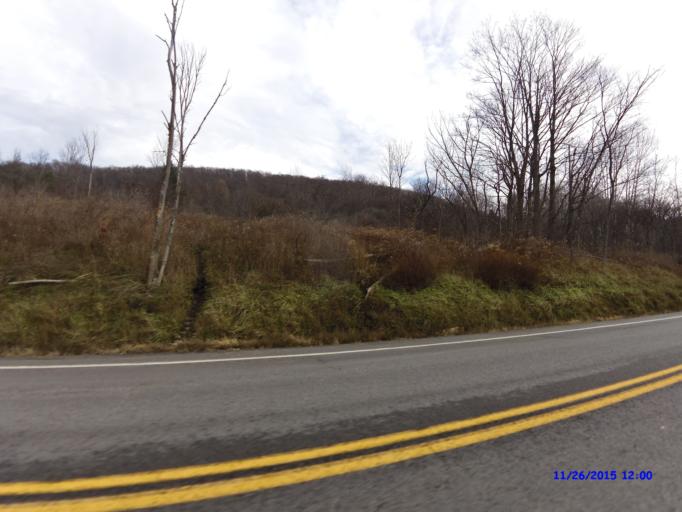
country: US
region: New York
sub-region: Cattaraugus County
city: Franklinville
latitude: 42.2838
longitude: -78.4517
